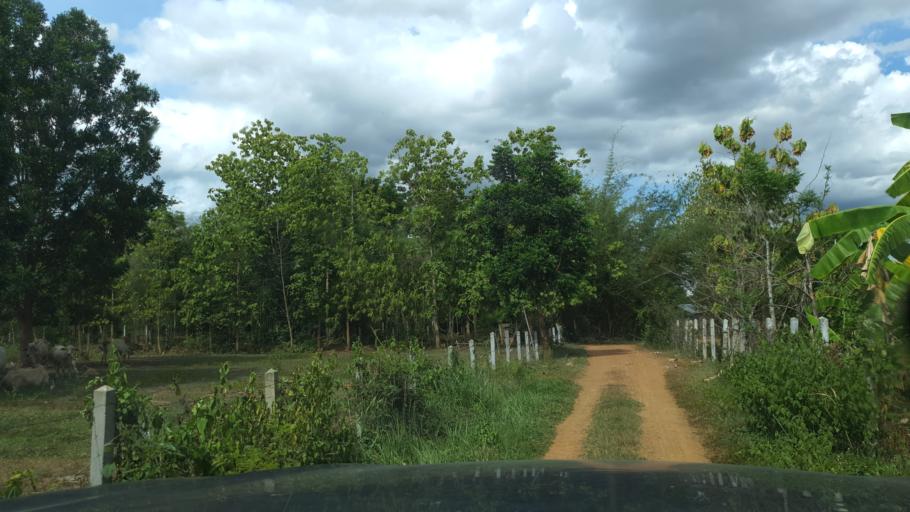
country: TH
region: Sukhothai
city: Thung Saliam
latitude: 17.3260
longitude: 99.5466
